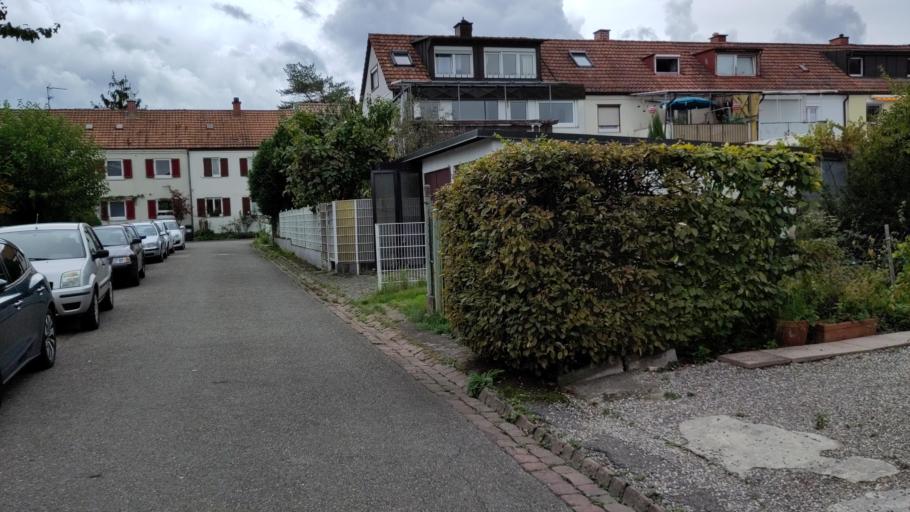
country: DE
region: Baden-Wuerttemberg
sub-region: Freiburg Region
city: Freiburg
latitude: 48.0133
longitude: 7.8297
